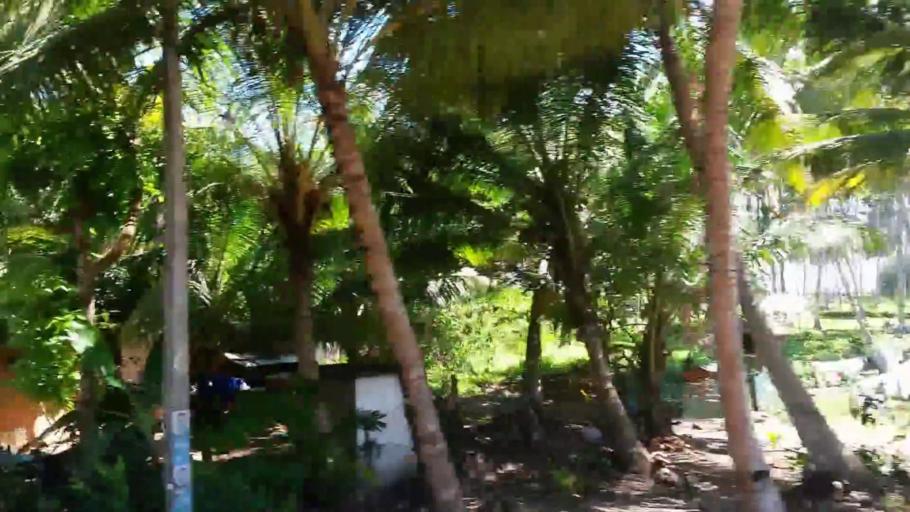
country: LK
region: Southern
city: Hikkaduwa
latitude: 6.1746
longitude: 80.0832
